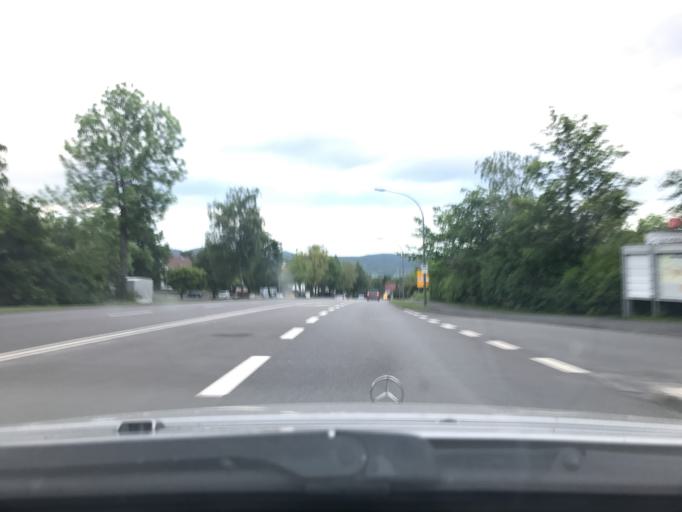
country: DE
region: Hesse
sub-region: Regierungsbezirk Kassel
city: Eschwege
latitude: 51.1825
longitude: 10.0405
